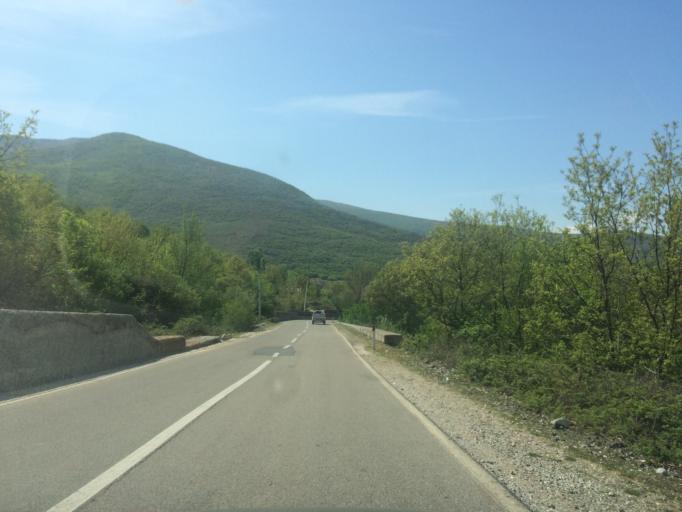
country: AL
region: Kukes
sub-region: Rrethi i Tropojes
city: Bytyc
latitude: 42.3914
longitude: 20.1800
